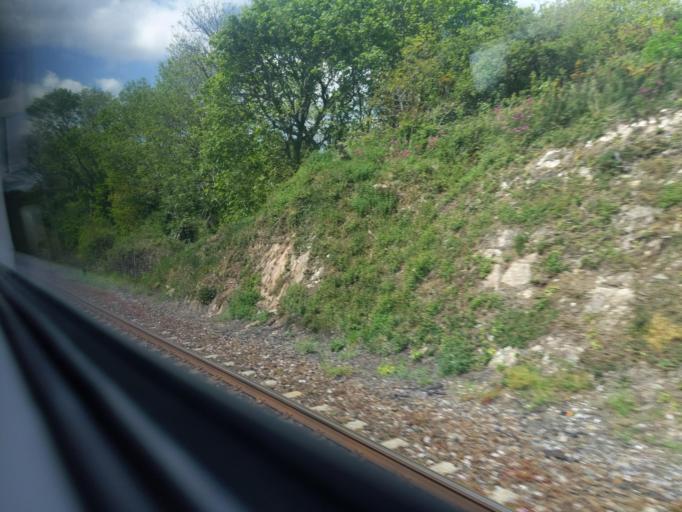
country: GB
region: England
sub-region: Cornwall
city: Saltash
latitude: 50.3976
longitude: -4.2273
